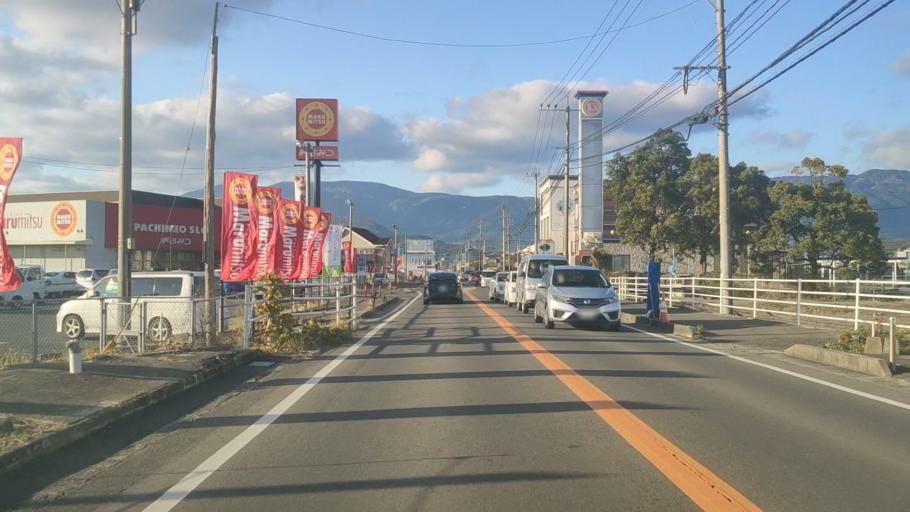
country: JP
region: Saga Prefecture
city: Saga-shi
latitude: 33.2784
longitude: 130.2142
